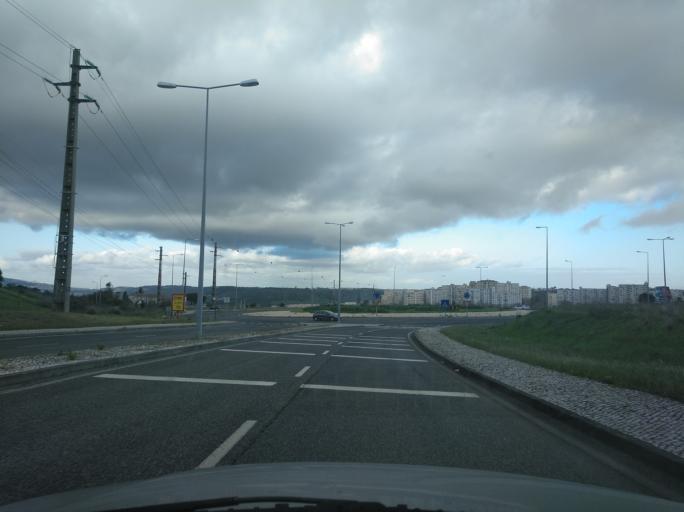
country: PT
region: Lisbon
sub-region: Loures
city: Loures
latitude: 38.8166
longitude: -9.1753
